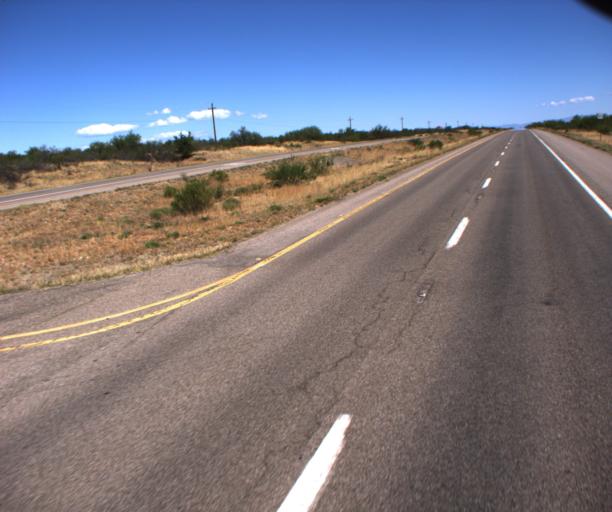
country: US
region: Arizona
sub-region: Cochise County
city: Whetstone
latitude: 31.8589
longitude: -110.3410
